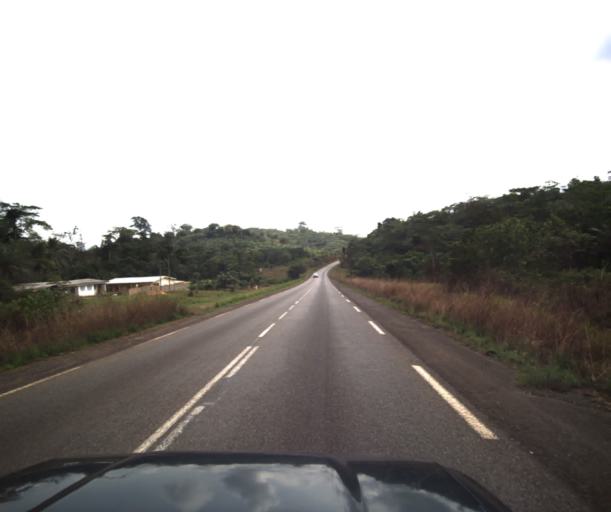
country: CM
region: Littoral
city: Edea
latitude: 3.8016
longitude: 10.2249
